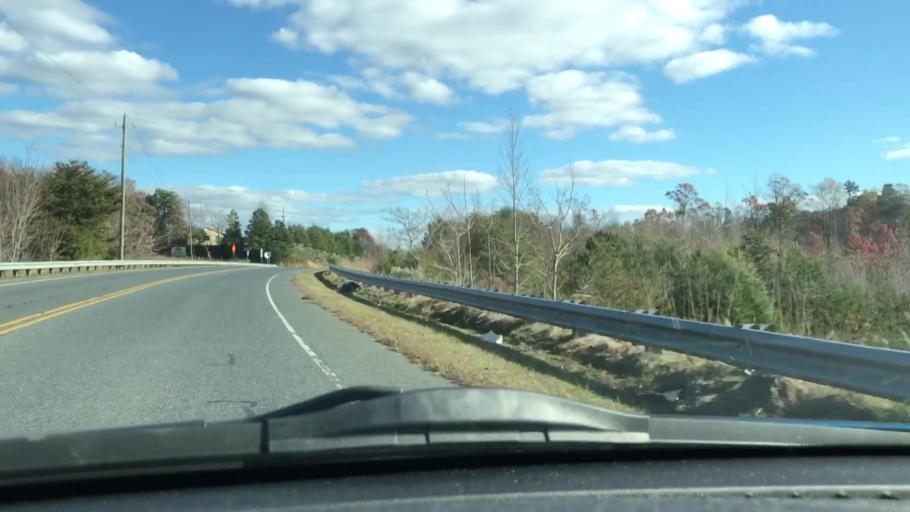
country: US
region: North Carolina
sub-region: Randolph County
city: Asheboro
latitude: 35.7164
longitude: -79.7922
